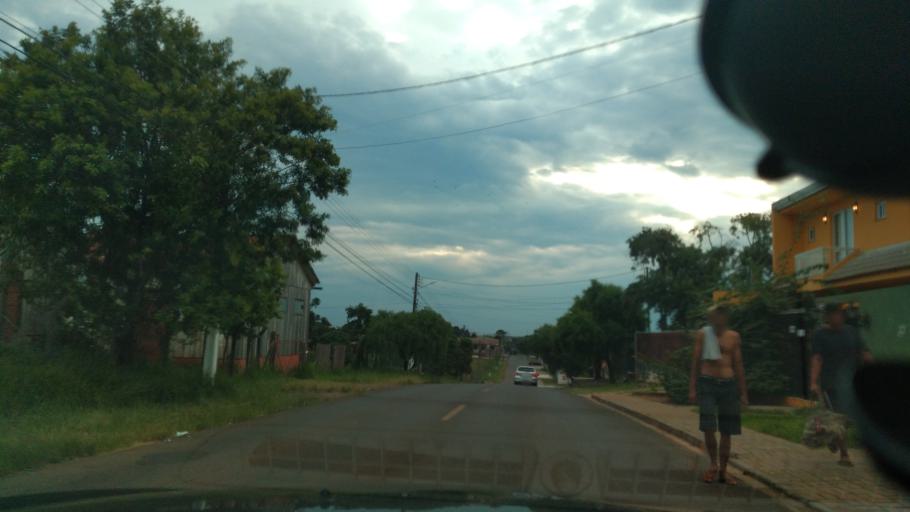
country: BR
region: Parana
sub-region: Guarapuava
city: Guarapuava
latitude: -25.3863
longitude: -51.4808
